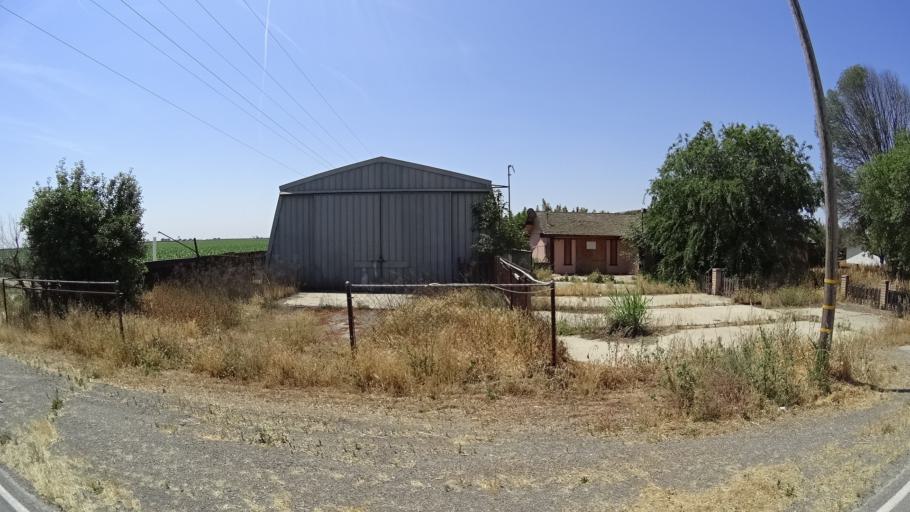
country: US
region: California
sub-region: Kings County
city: Lucerne
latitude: 36.4013
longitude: -119.5922
